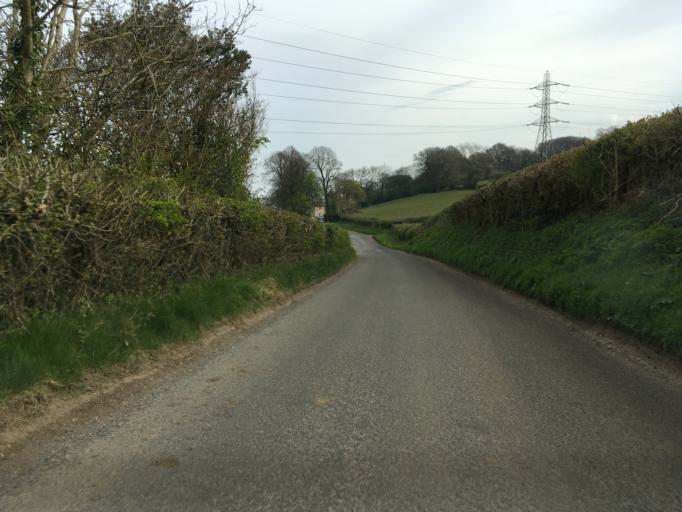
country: GB
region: Wales
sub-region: Cardiff
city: Radyr
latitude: 51.5387
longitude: -3.2333
